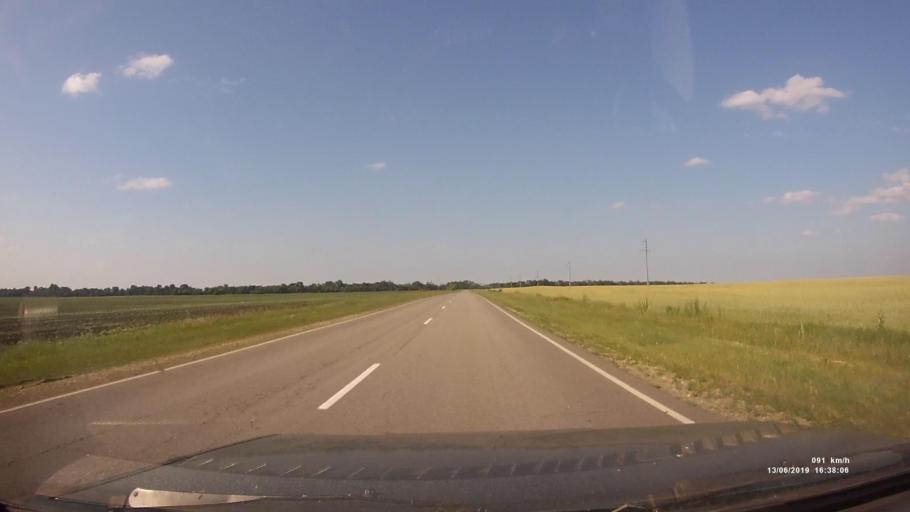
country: RU
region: Rostov
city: Kazanskaya
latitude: 49.9148
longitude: 41.3203
